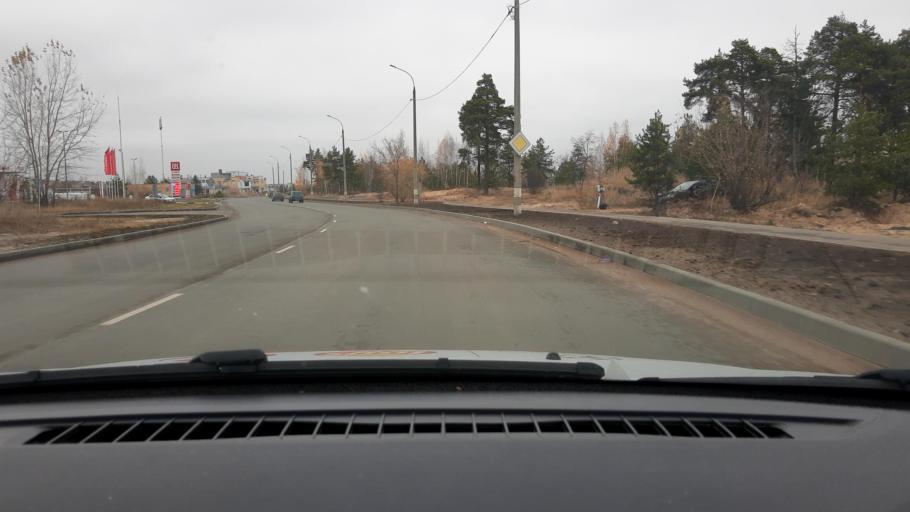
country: RU
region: Nizjnij Novgorod
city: Dzerzhinsk
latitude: 56.2361
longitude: 43.4081
